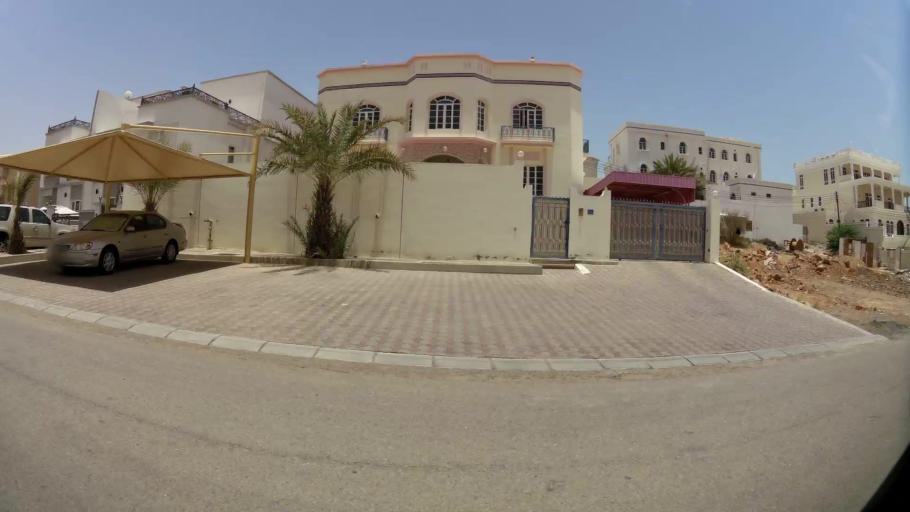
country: OM
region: Muhafazat Masqat
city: Bawshar
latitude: 23.5572
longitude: 58.4163
